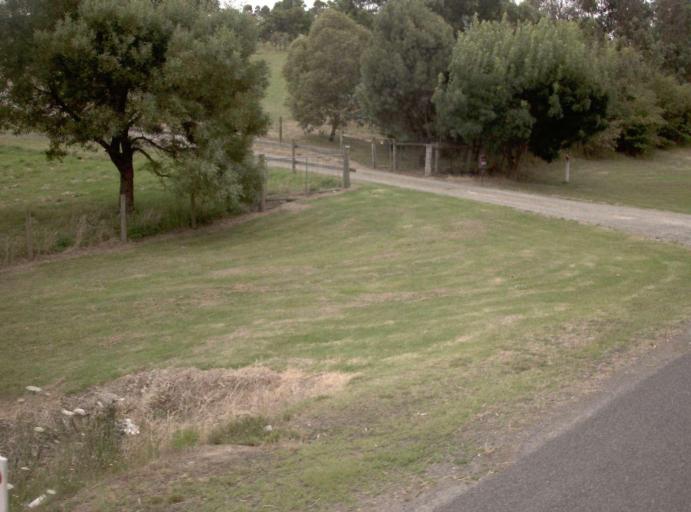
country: AU
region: Victoria
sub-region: Yarra Ranges
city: Yarra Glen
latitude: -37.6506
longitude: 145.3818
